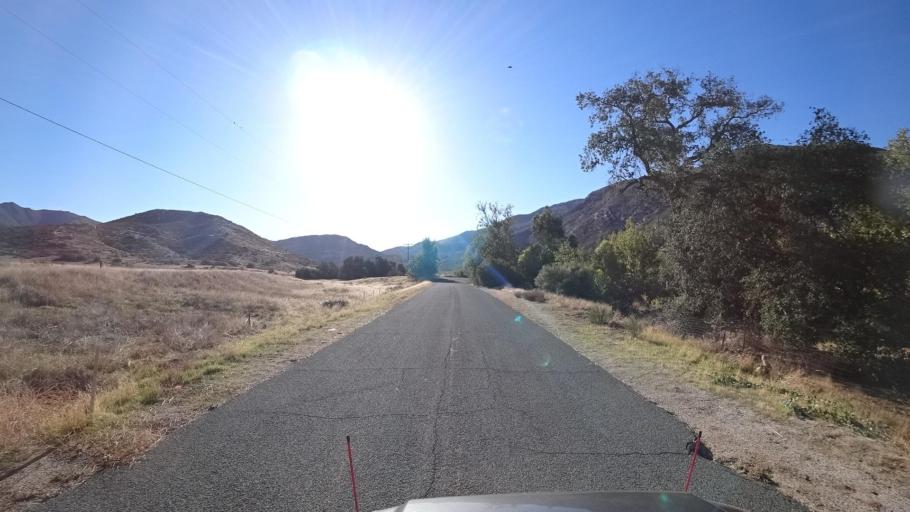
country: MX
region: Baja California
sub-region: Tecate
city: Lomas de Santa Anita
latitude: 32.6092
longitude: -116.6967
